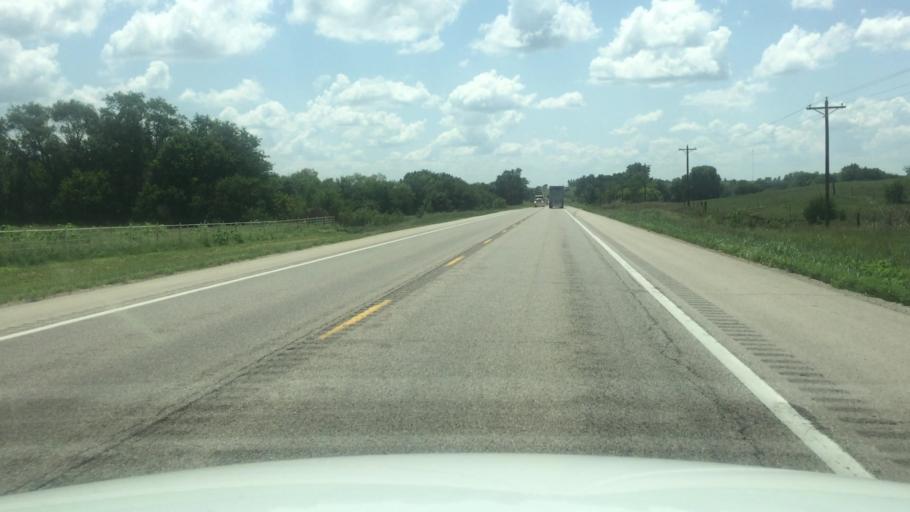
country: US
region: Kansas
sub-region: Brown County
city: Horton
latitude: 39.6938
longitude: -95.7303
